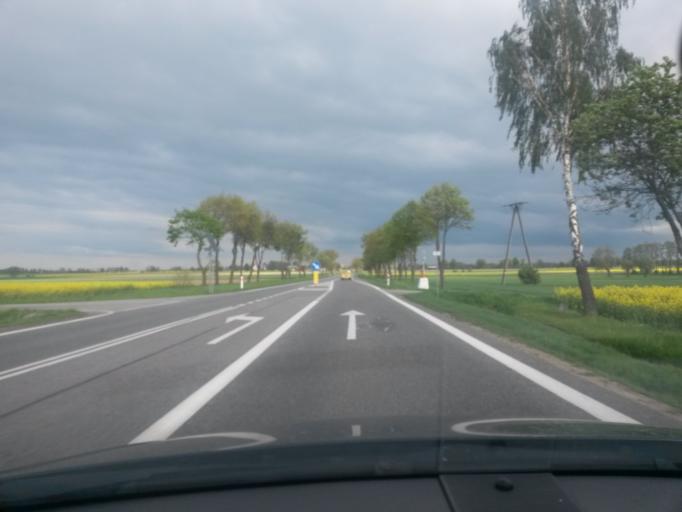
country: PL
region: Masovian Voivodeship
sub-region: Powiat plonski
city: Dzierzaznia
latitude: 52.6325
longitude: 20.1738
